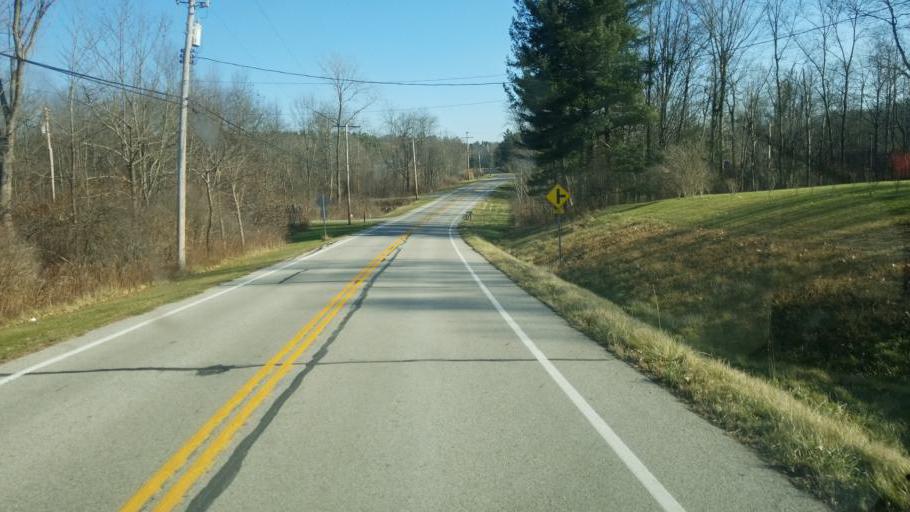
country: US
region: Ohio
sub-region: Geauga County
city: Burton
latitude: 41.4753
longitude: -81.2160
